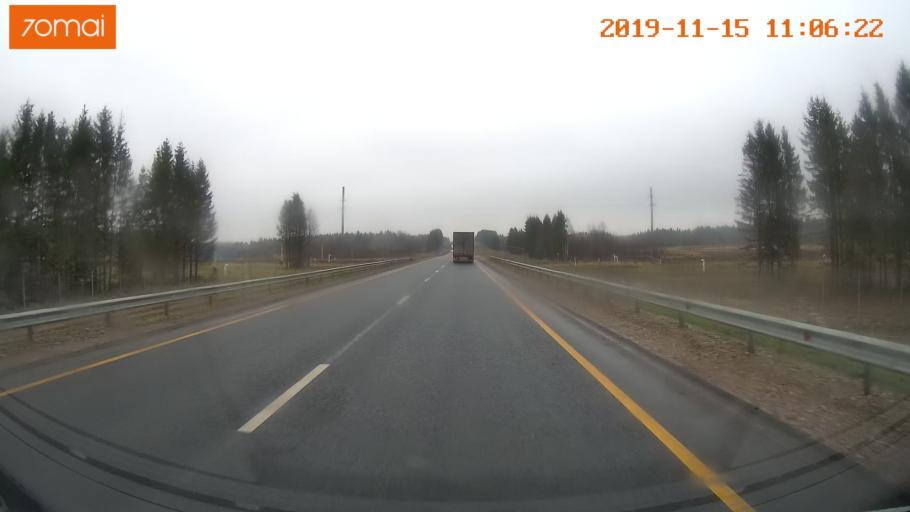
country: RU
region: Vologda
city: Chebsara
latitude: 59.1190
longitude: 39.0258
